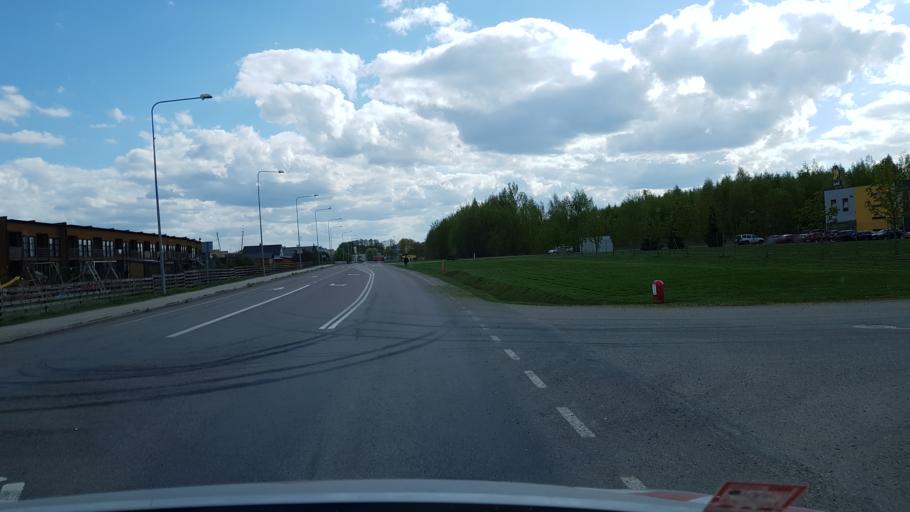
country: EE
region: Tartu
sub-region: Tartu linn
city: Tartu
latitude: 58.3821
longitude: 26.7791
